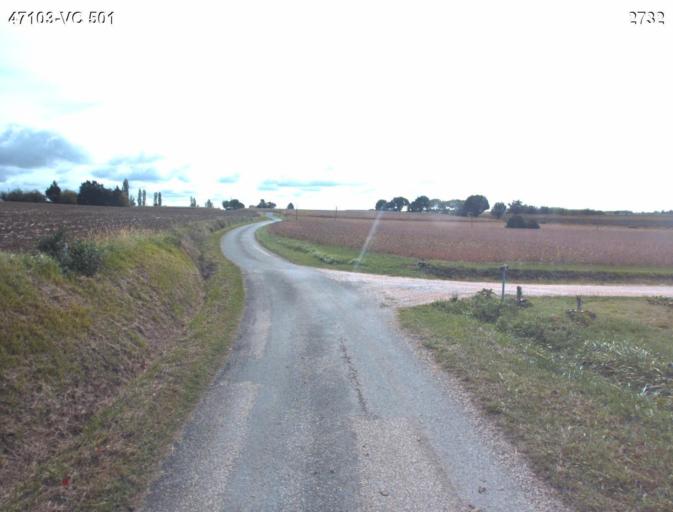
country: FR
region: Aquitaine
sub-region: Departement du Lot-et-Garonne
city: Nerac
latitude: 44.0995
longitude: 0.3224
